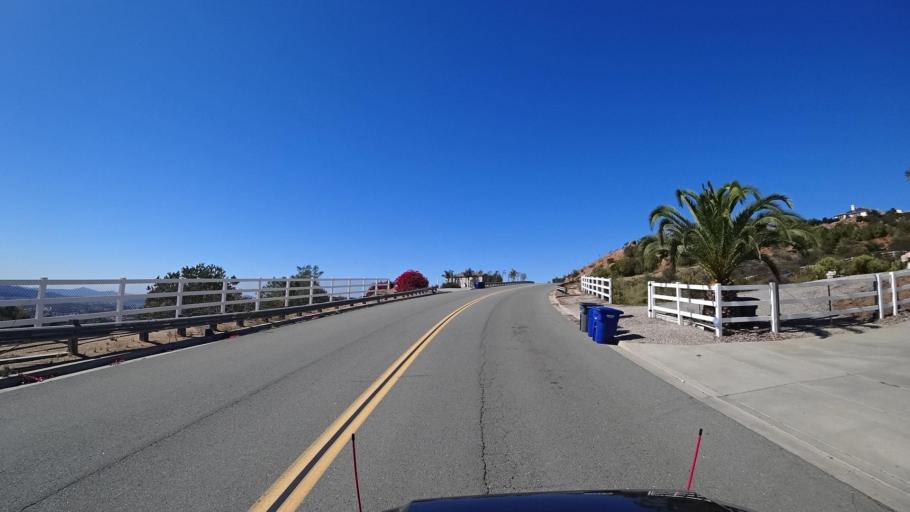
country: US
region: California
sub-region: San Diego County
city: Harbison Canyon
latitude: 32.8793
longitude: -116.8377
